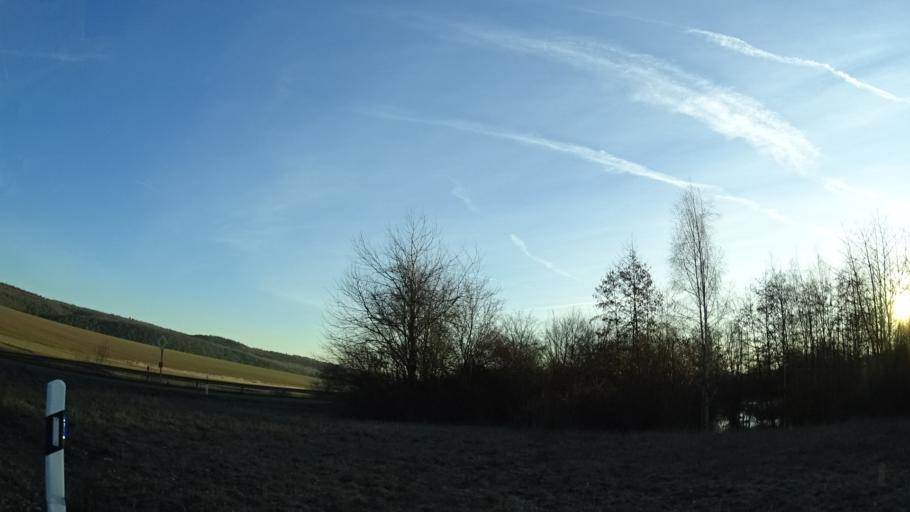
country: DE
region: Rheinland-Pfalz
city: Dannenfels
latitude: 49.6421
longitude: 7.9736
